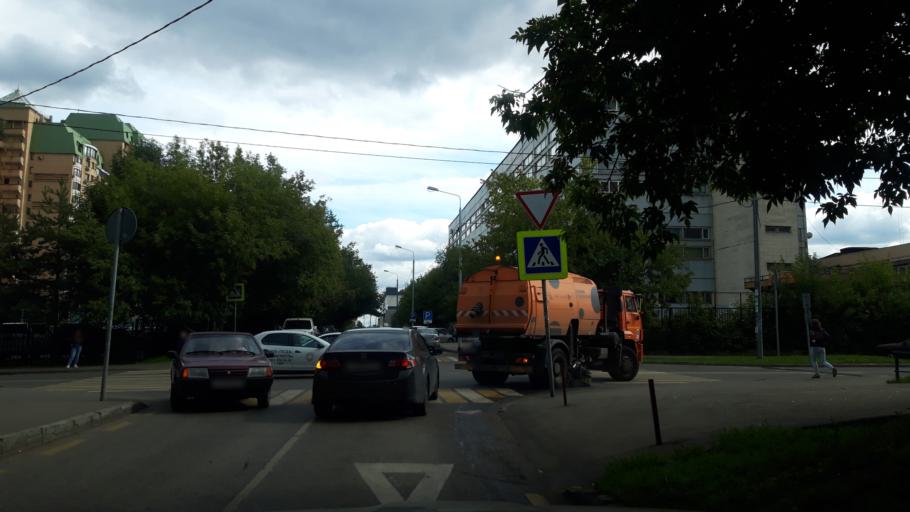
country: RU
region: Moskovskaya
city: Levoberezhnyy
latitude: 55.8446
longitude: 37.4830
